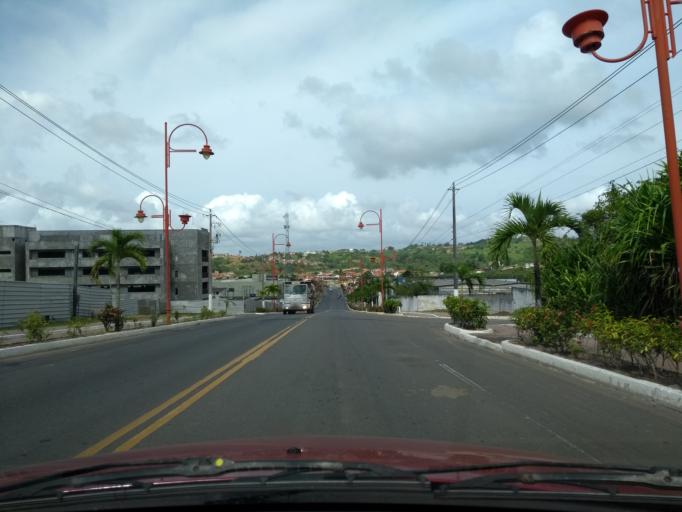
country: BR
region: Bahia
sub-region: Sao Francisco Do Conde
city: Sao Francisco do Conde
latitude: -12.6157
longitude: -38.6608
